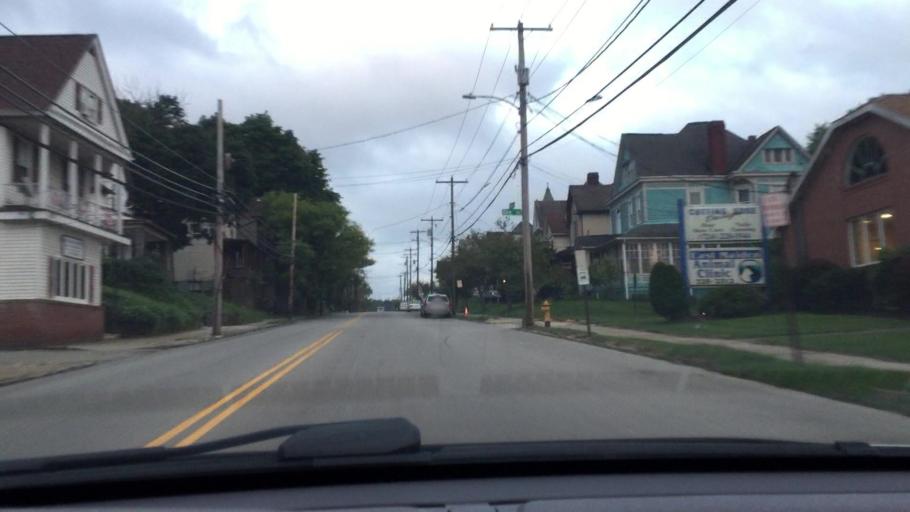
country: US
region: Pennsylvania
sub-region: Washington County
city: East Washington
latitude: 40.1658
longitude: -80.2336
